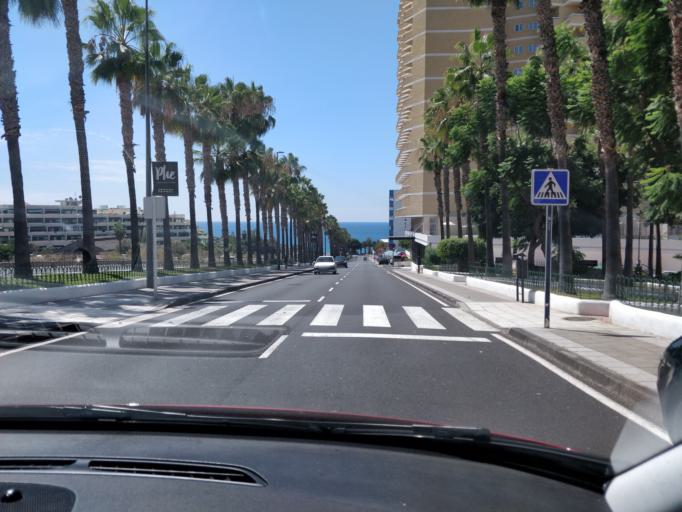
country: ES
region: Canary Islands
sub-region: Provincia de Santa Cruz de Tenerife
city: Puerto de la Cruz
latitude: 28.4109
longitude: -16.5555
